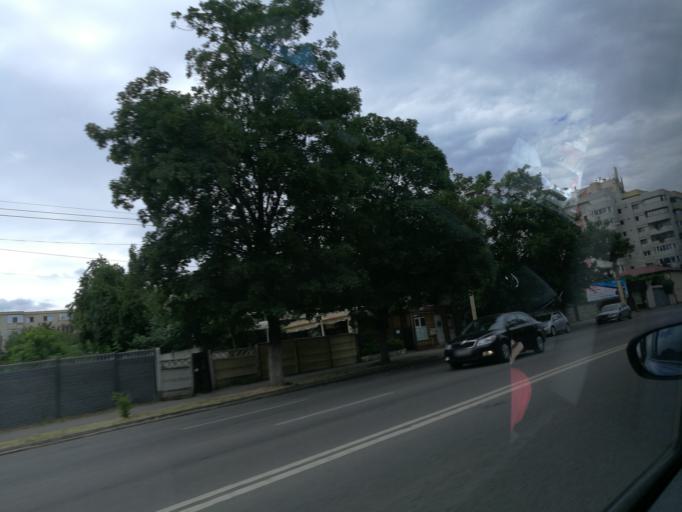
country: RO
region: Constanta
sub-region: Municipiul Constanta
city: Constanta
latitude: 44.1629
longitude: 28.6323
